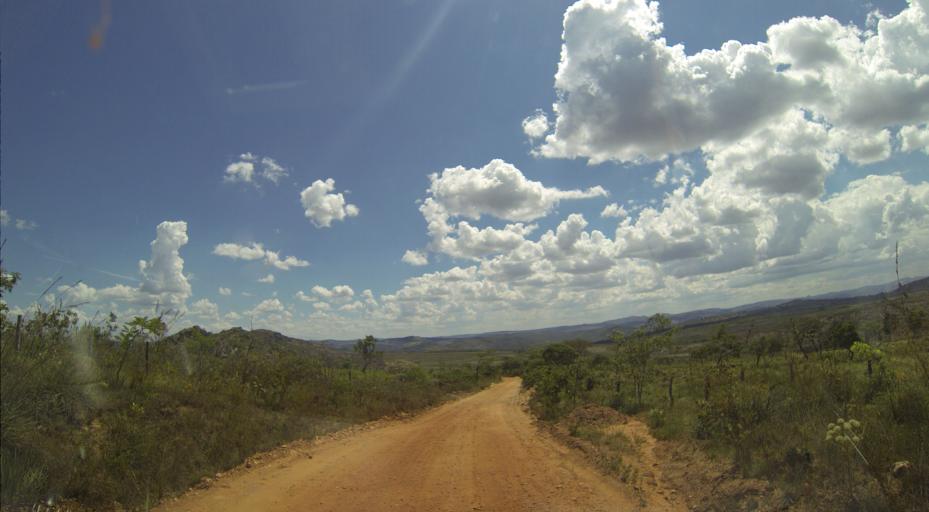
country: BR
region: Minas Gerais
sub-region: Serro
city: Serro
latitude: -18.4708
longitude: -43.4550
